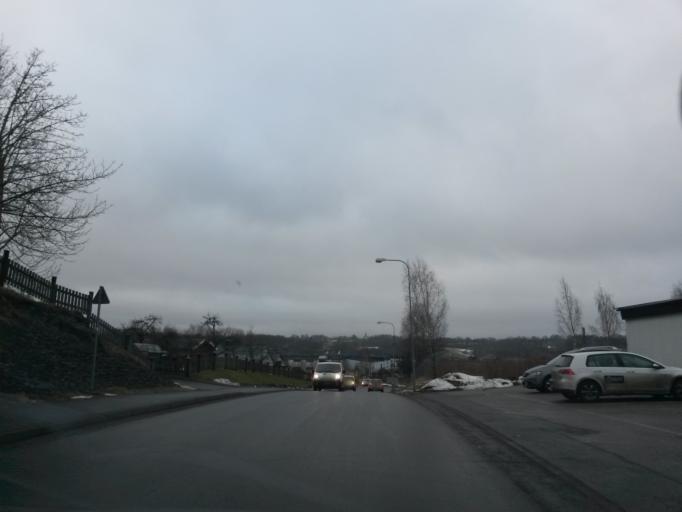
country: SE
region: Vaestra Goetaland
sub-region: Marks Kommun
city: Kinna
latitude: 57.4961
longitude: 12.6674
